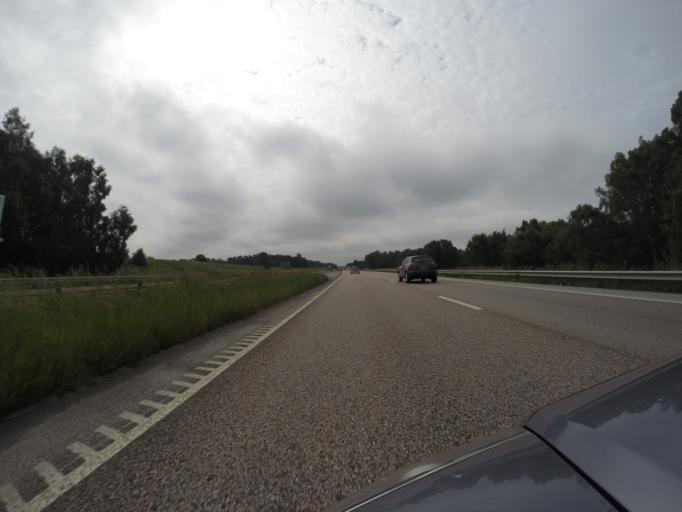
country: SE
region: Skane
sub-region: Kavlinge Kommun
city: Hofterup
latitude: 55.8151
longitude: 12.9414
